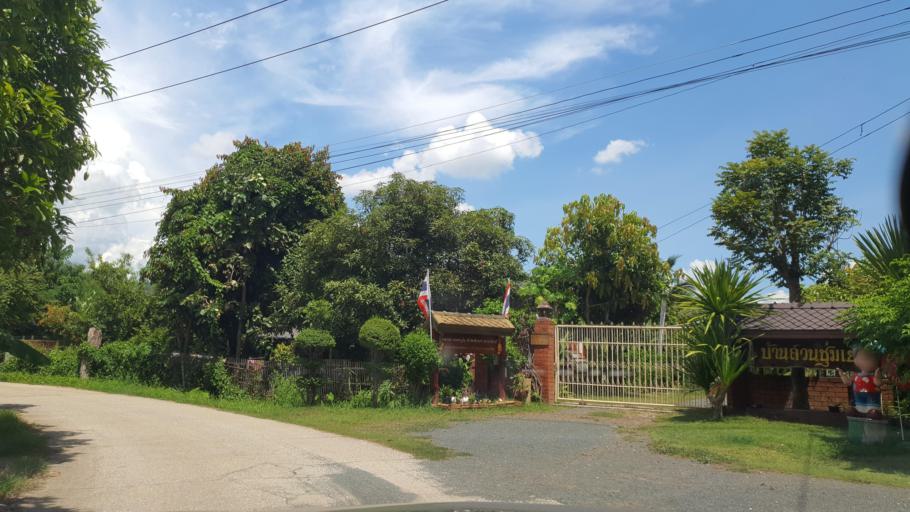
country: TH
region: Chiang Mai
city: Mae On
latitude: 18.7847
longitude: 99.1858
